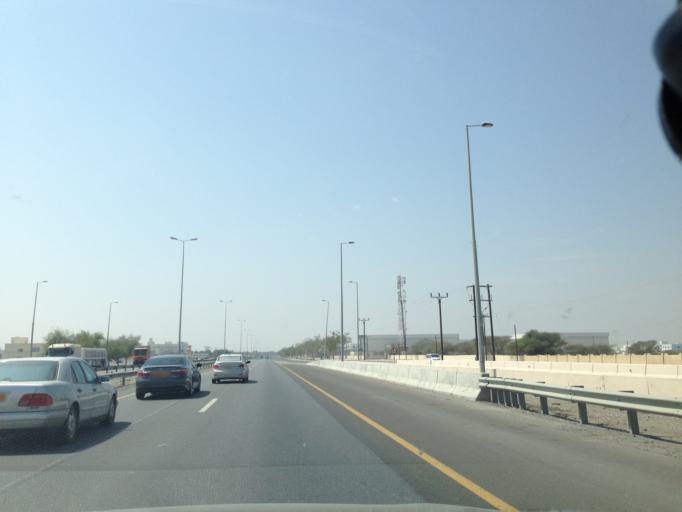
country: OM
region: Al Batinah
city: Barka'
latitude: 23.6625
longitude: 57.9457
